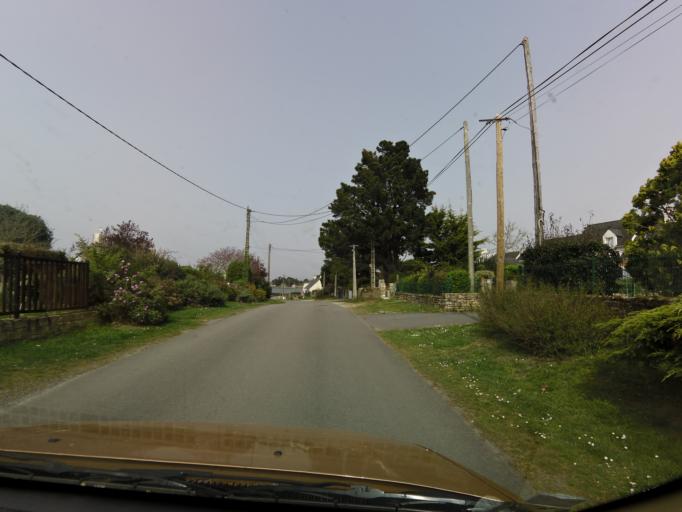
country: FR
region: Brittany
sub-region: Departement du Morbihan
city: Sene
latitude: 47.5840
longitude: -2.7171
